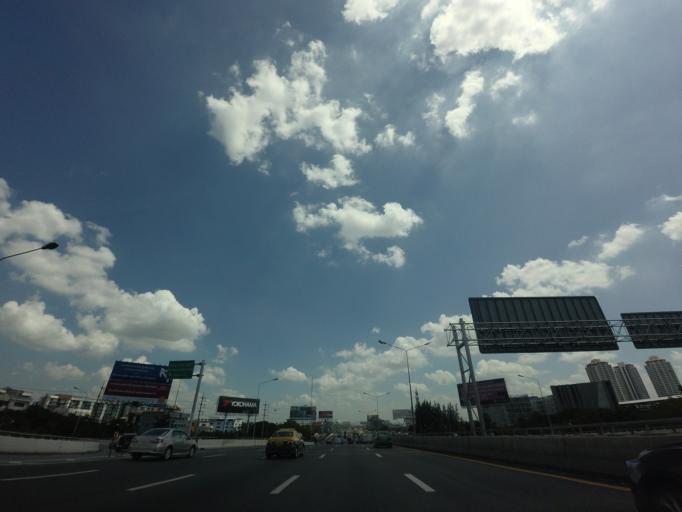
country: TH
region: Bangkok
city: Suan Luang
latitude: 13.7413
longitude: 100.6430
